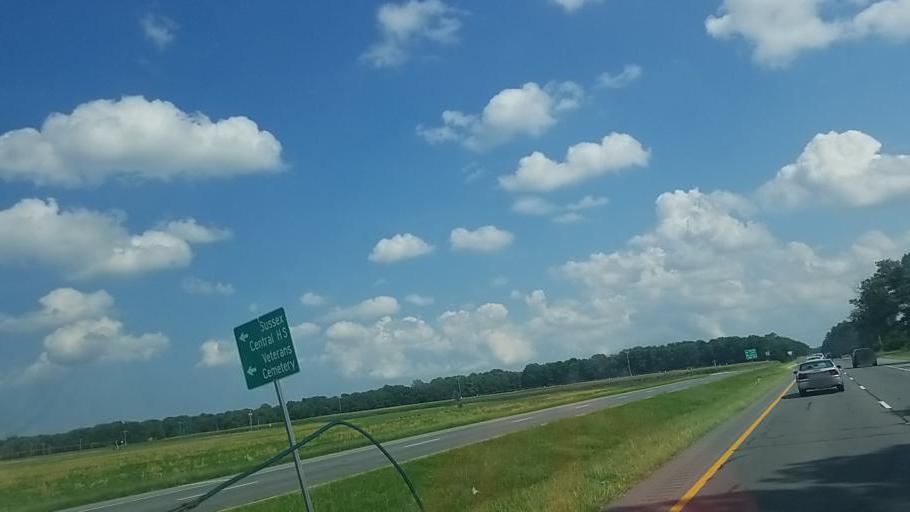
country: US
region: Delaware
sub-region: Sussex County
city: Millsboro
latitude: 38.6198
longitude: -75.3368
